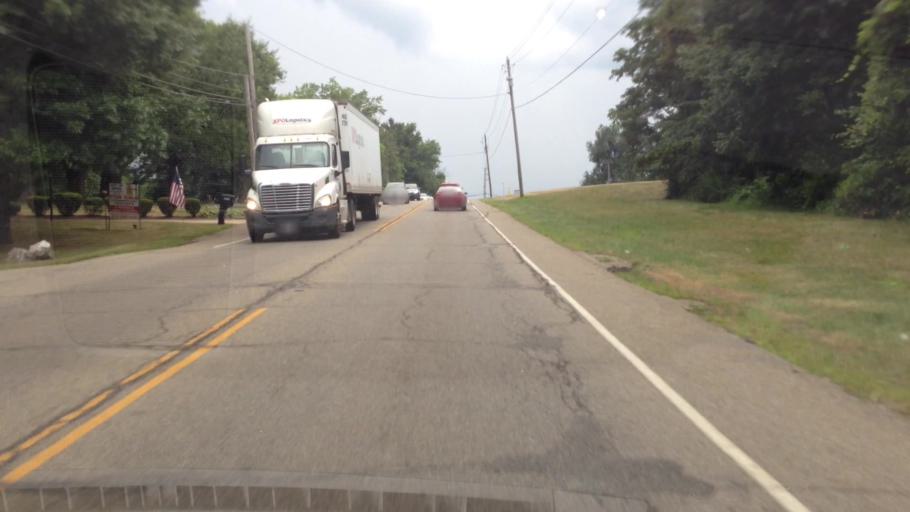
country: US
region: Ohio
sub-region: Summit County
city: Green
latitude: 40.9701
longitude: -81.4649
